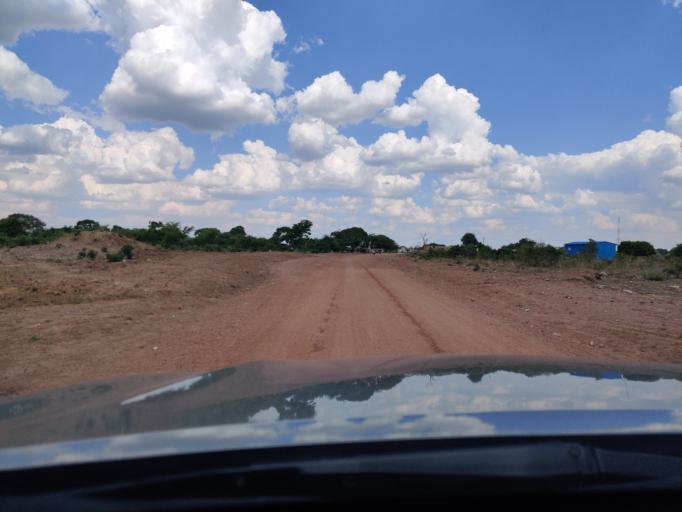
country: ZM
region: Central
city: Chibombo
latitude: -14.7615
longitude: 27.8971
